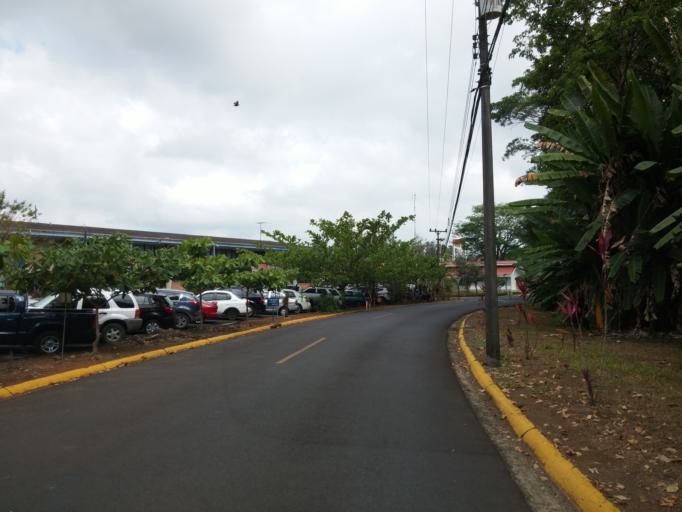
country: CR
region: Alajuela
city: Quesada
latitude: 10.3616
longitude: -84.5089
